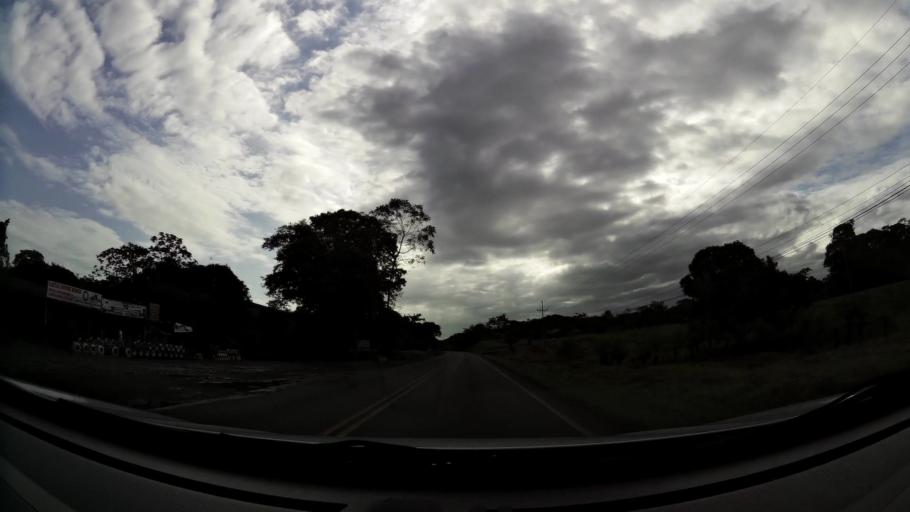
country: CR
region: Limon
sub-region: Canton de Guacimo
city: Guacimo
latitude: 10.2025
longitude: -83.6780
